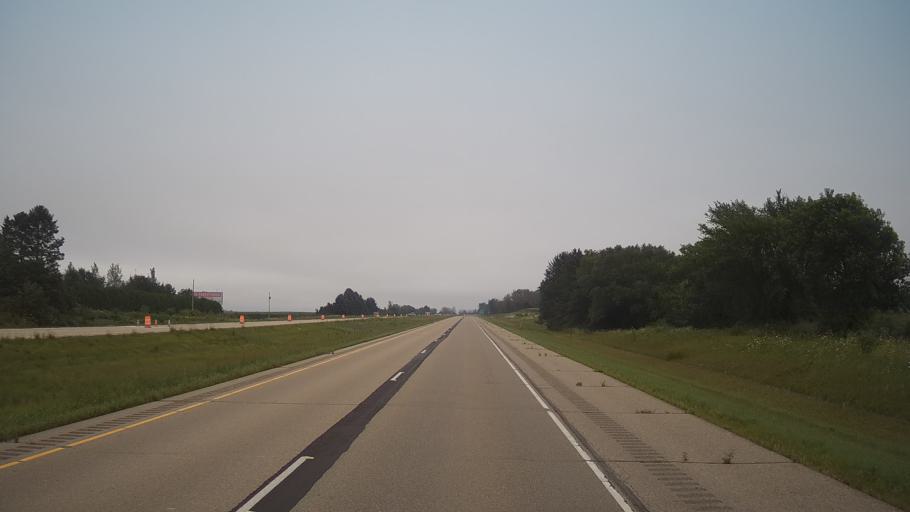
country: US
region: Minnesota
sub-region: Olmsted County
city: Stewartville
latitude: 43.8691
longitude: -92.5160
